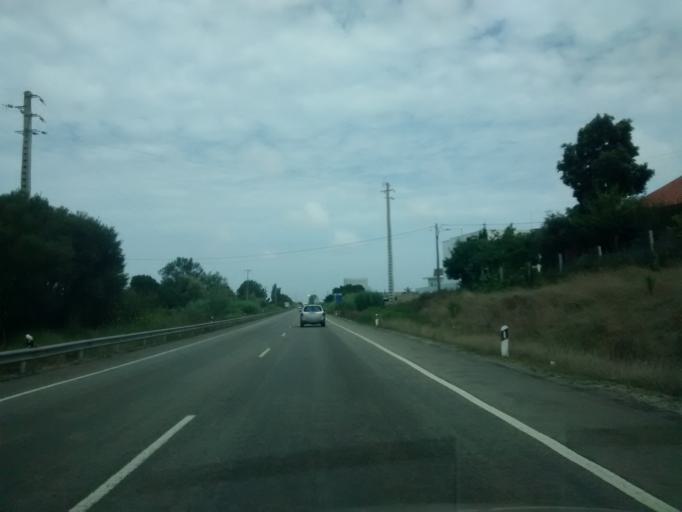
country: PT
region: Aveiro
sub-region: Aveiro
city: Aradas
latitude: 40.6161
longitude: -8.6365
